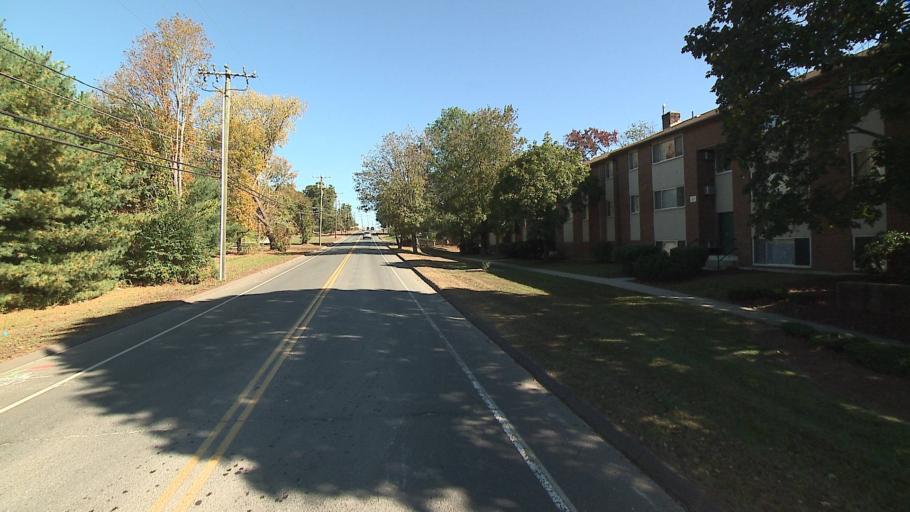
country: US
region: Connecticut
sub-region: Windham County
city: Willimantic
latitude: 41.7228
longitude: -72.1932
